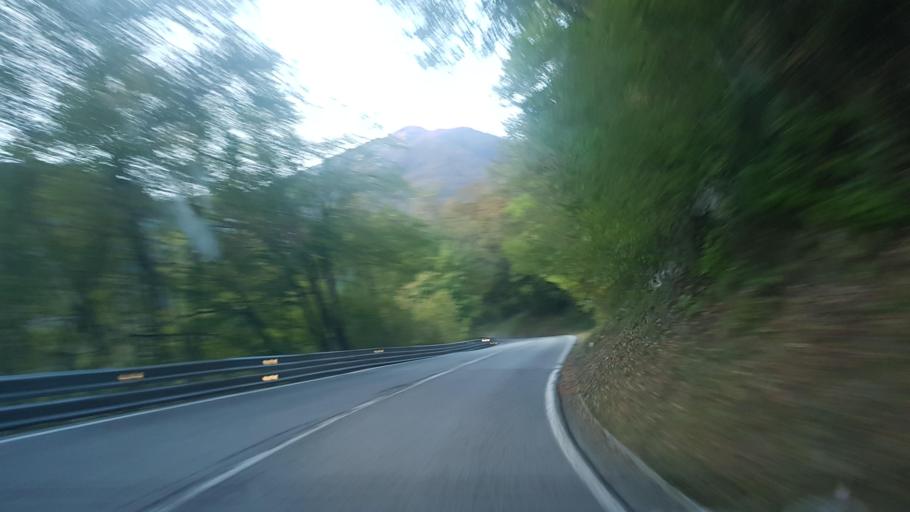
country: IT
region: Friuli Venezia Giulia
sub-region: Provincia di Udine
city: Chiaulis
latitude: 46.3708
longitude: 12.9660
